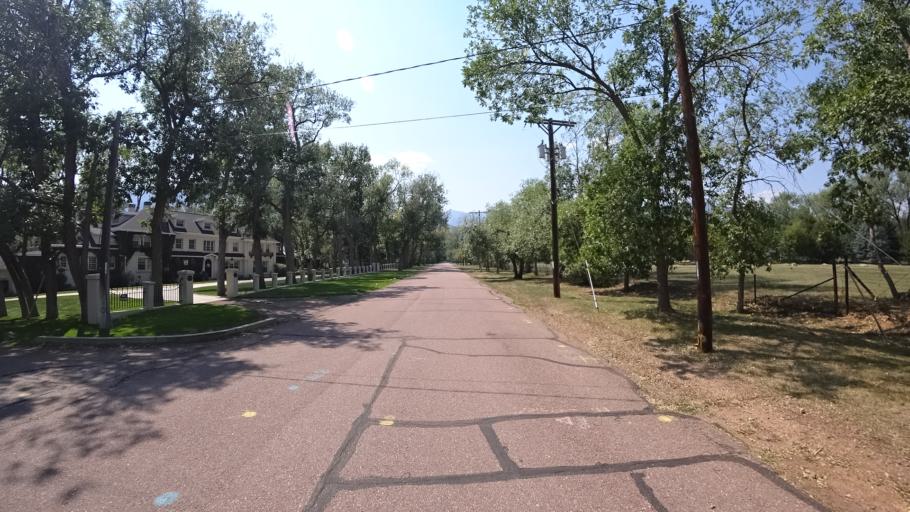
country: US
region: Colorado
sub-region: El Paso County
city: Colorado Springs
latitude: 38.7908
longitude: -104.8424
